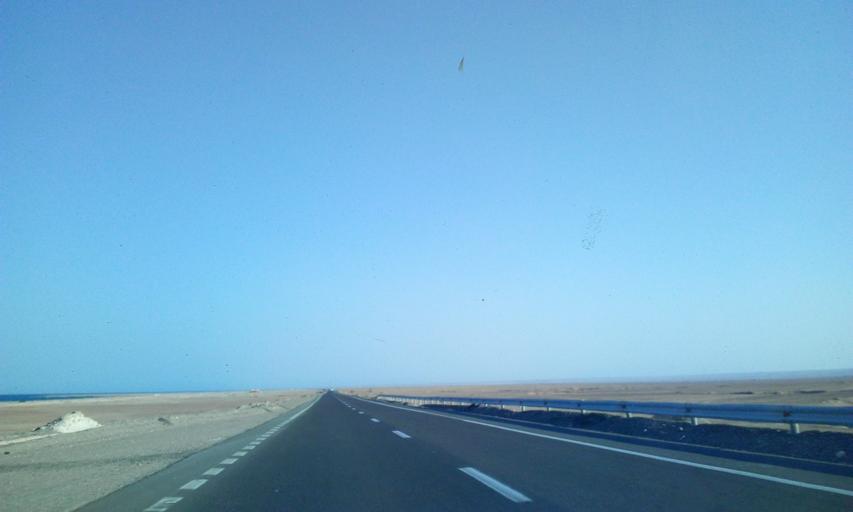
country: EG
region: South Sinai
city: Tor
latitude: 28.6644
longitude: 32.8391
